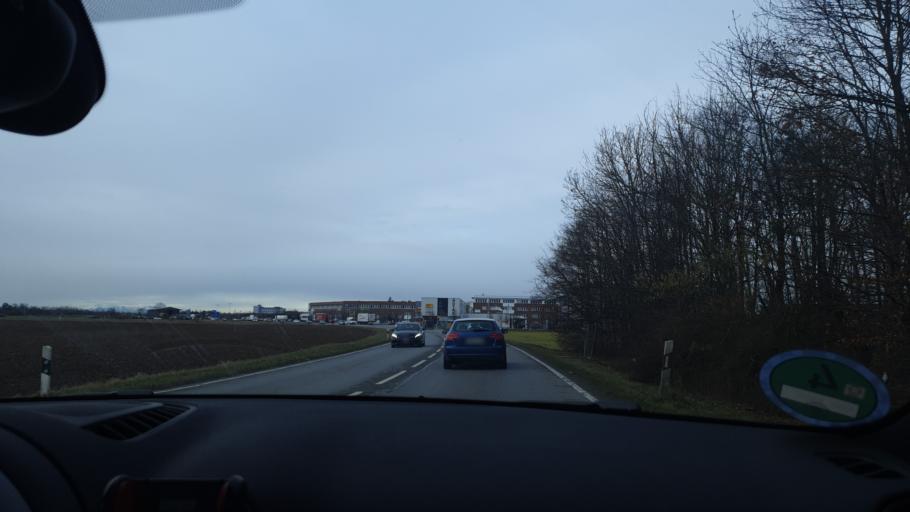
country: DE
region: Bavaria
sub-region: Upper Bavaria
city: Feldkirchen
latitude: 48.1500
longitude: 11.7485
